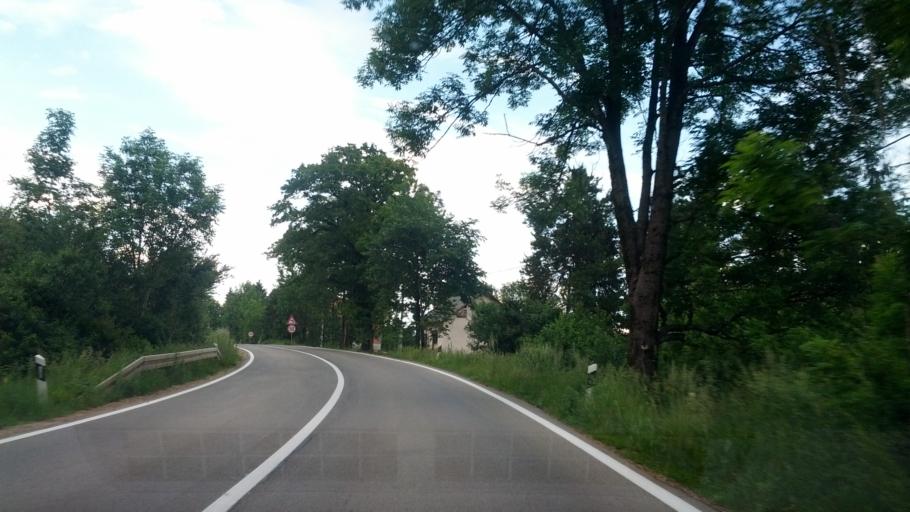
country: BA
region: Federation of Bosnia and Herzegovina
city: Izacic
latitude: 44.8833
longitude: 15.7259
